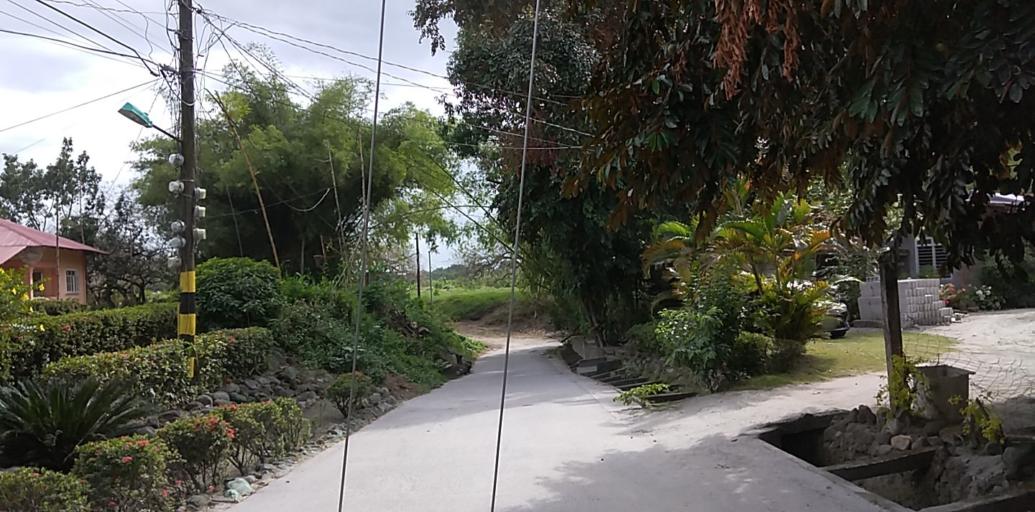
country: PH
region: Central Luzon
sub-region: Province of Pampanga
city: Pulung Santol
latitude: 15.0443
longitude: 120.5555
